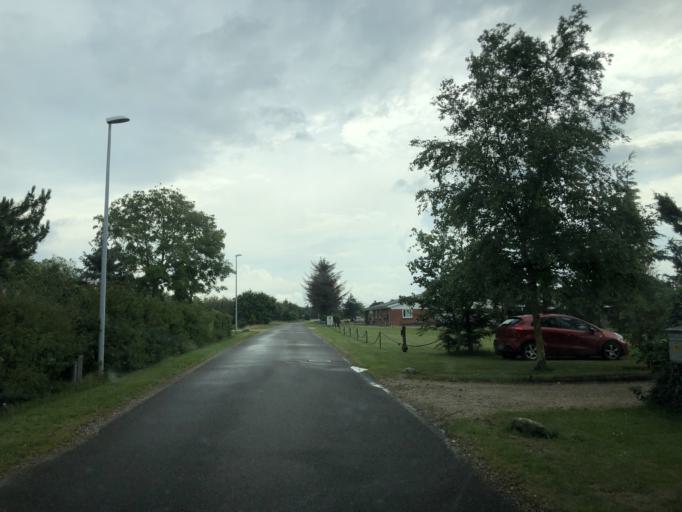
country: DK
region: Central Jutland
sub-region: Ringkobing-Skjern Kommune
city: Skjern
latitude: 55.8904
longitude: 8.4137
